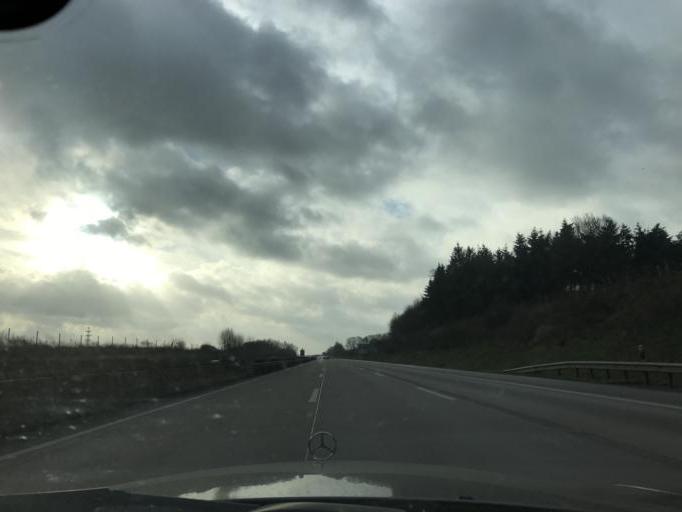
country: DE
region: Lower Saxony
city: Buehren
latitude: 52.8340
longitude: 8.2167
